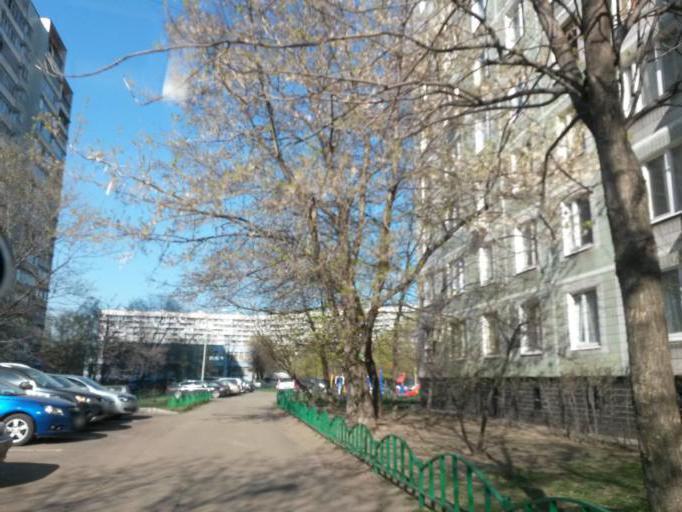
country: RU
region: Moscow
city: Mar'ino
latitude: 55.6481
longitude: 37.7203
